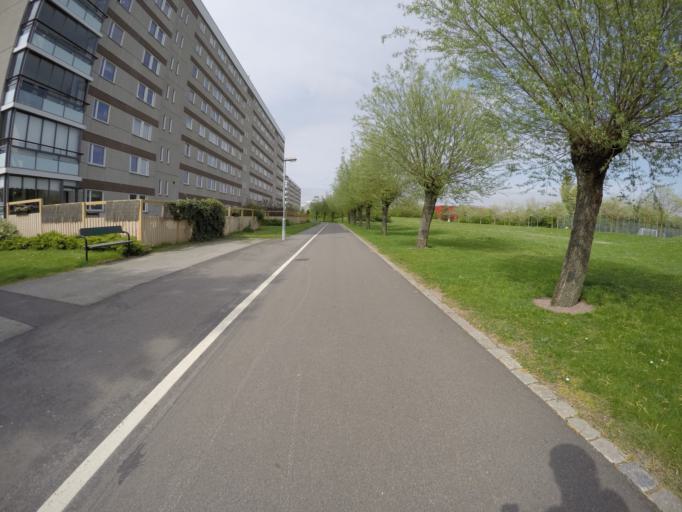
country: SE
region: Skane
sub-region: Malmo
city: Tygelsjo
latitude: 55.5601
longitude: 12.9886
